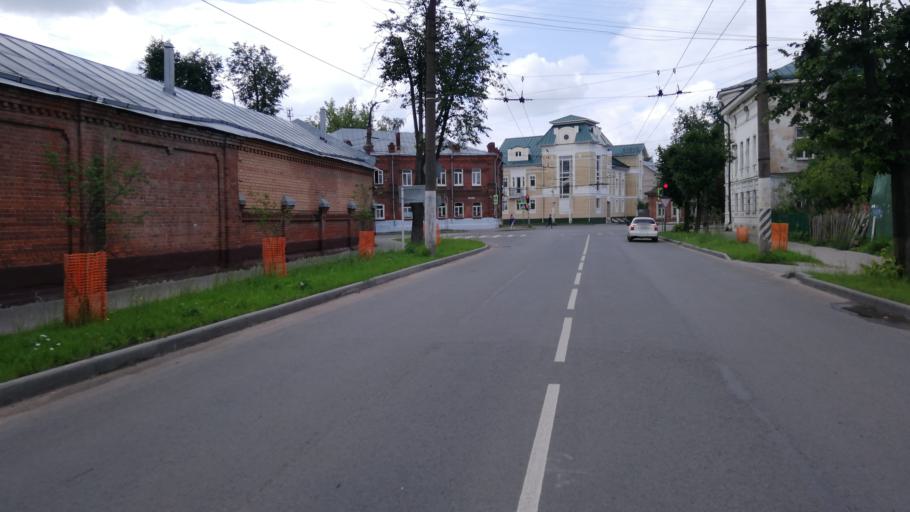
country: RU
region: Kostroma
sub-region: Kostromskoy Rayon
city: Kostroma
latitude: 57.7720
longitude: 40.9310
